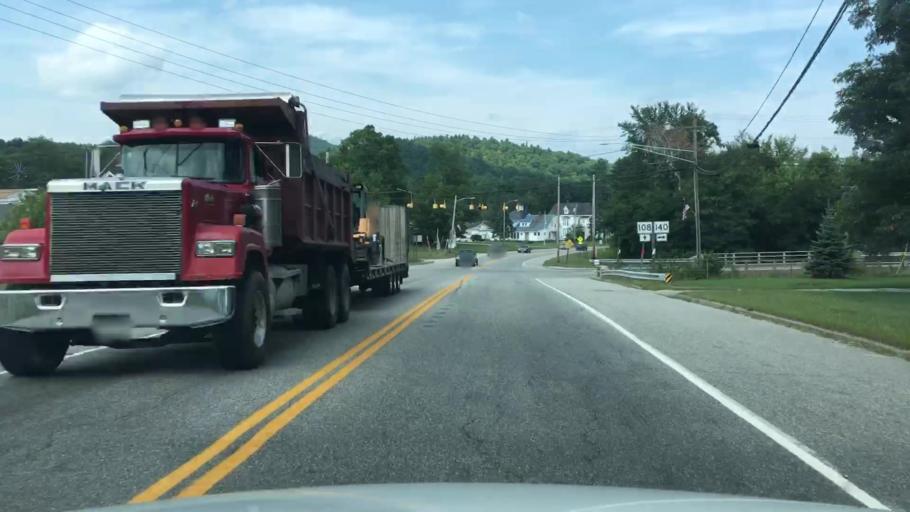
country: US
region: Maine
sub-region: Oxford County
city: Canton
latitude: 44.4401
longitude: -70.3147
